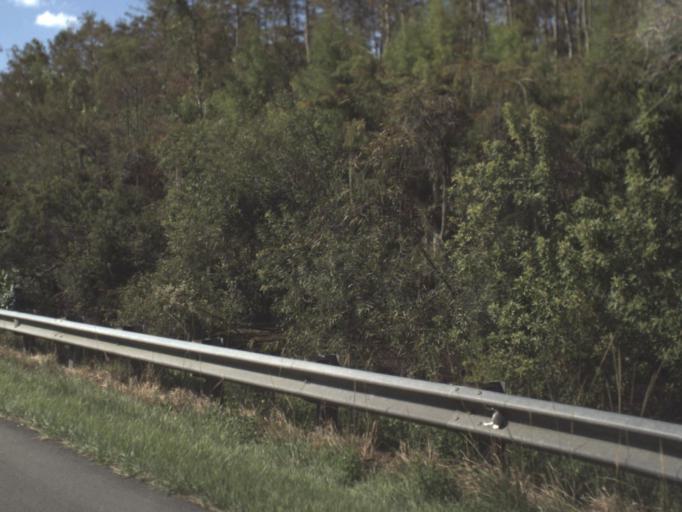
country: US
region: Florida
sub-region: Miami-Dade County
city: Kendall West
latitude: 25.8559
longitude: -81.0240
